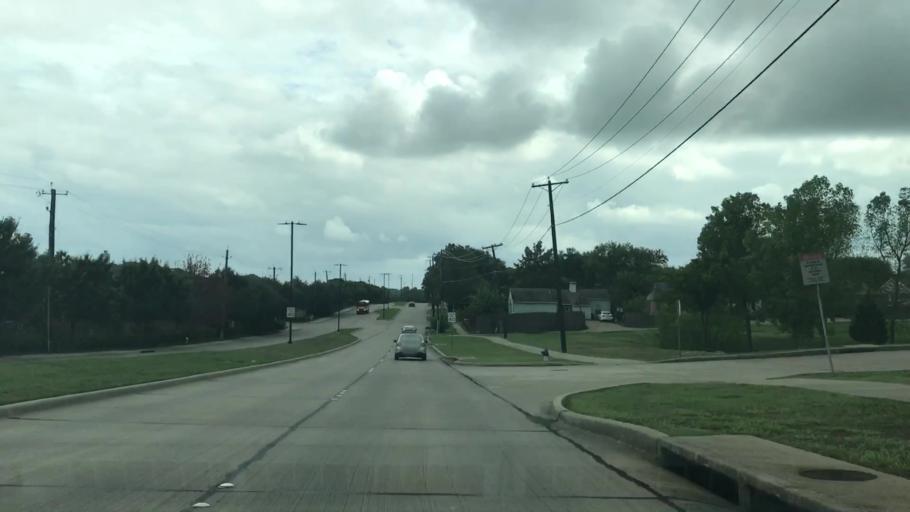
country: US
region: Texas
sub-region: Dallas County
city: Garland
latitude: 32.8935
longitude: -96.6137
